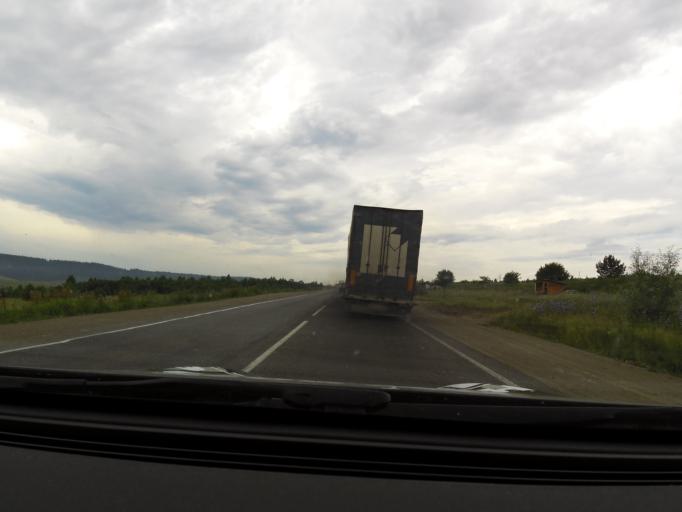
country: RU
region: Chelyabinsk
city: Sim
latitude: 55.0052
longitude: 57.6735
